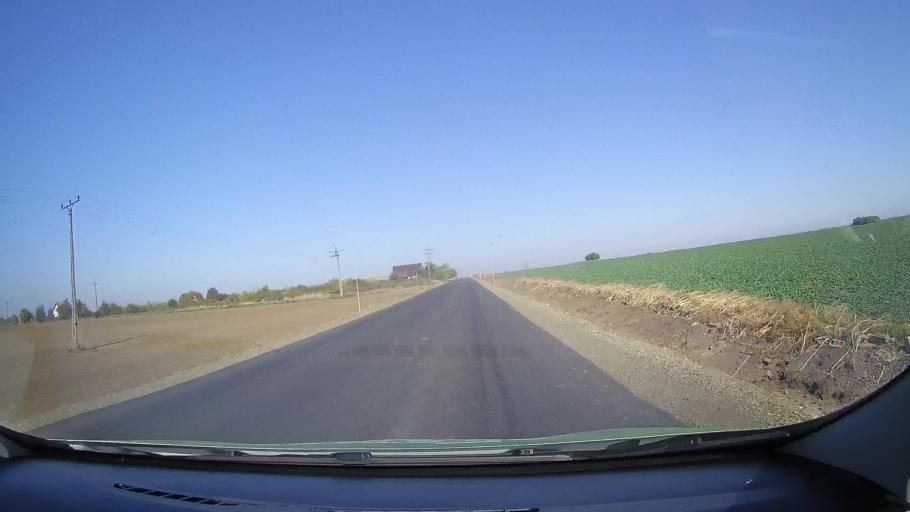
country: RO
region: Satu Mare
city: Carei
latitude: 47.6562
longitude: 22.4607
